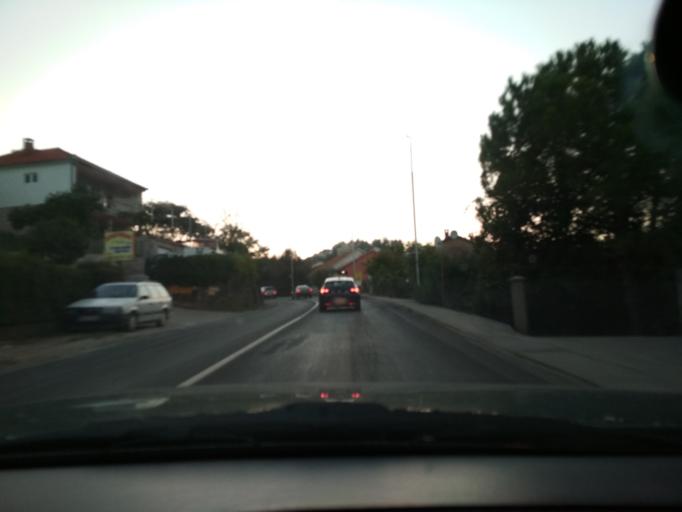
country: ME
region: Herceg Novi
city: Herceg-Novi
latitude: 42.4539
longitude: 18.5431
